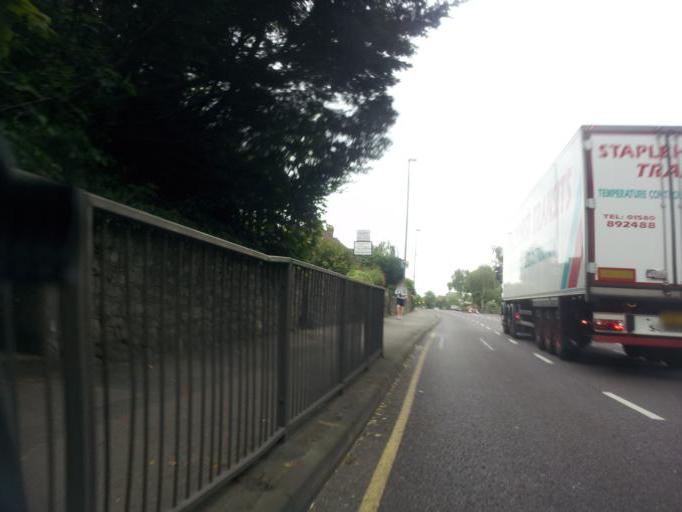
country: GB
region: England
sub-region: Kent
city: Maidstone
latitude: 51.2639
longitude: 0.5284
